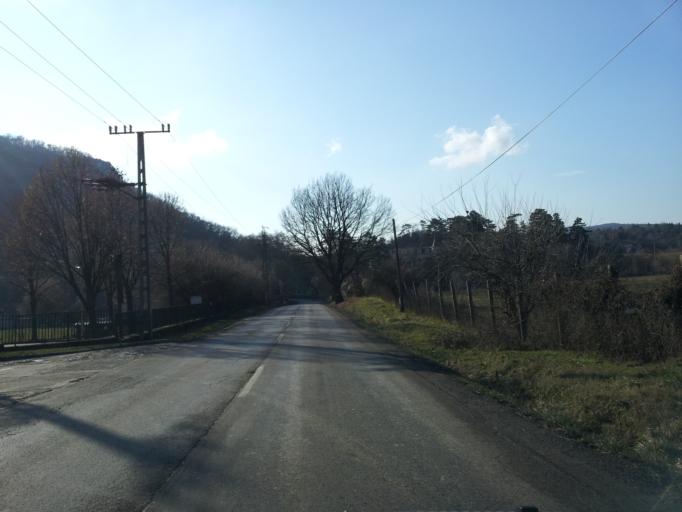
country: HU
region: Pest
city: Csobanka
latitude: 47.6556
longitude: 18.9769
